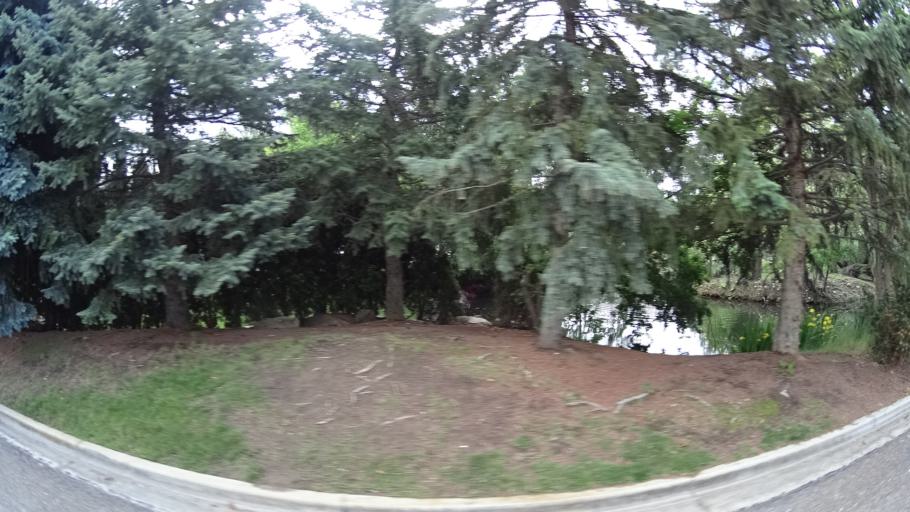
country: US
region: Idaho
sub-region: Ada County
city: Eagle
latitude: 43.6708
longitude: -116.2971
